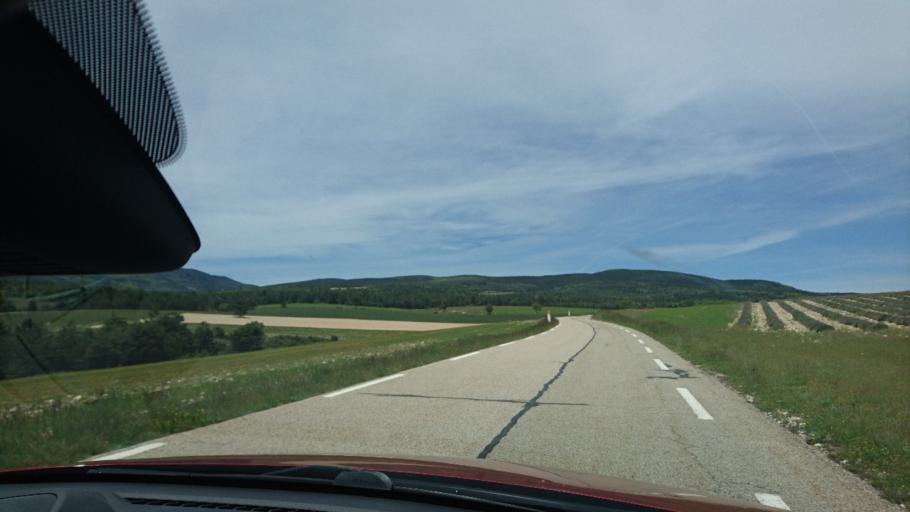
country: FR
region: Provence-Alpes-Cote d'Azur
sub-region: Departement du Vaucluse
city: Sault
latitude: 44.1115
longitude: 5.3888
